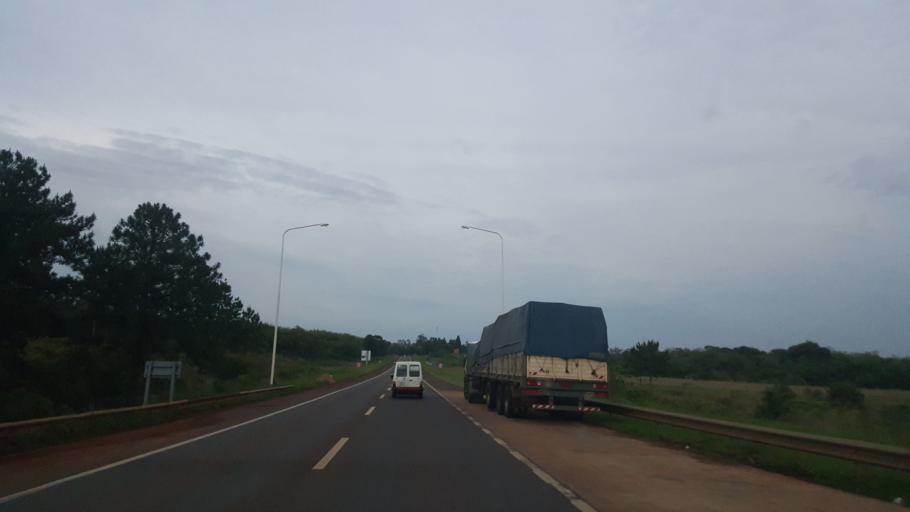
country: AR
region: Misiones
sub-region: Departamento de Apostoles
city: San Jose
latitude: -27.7844
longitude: -55.8231
